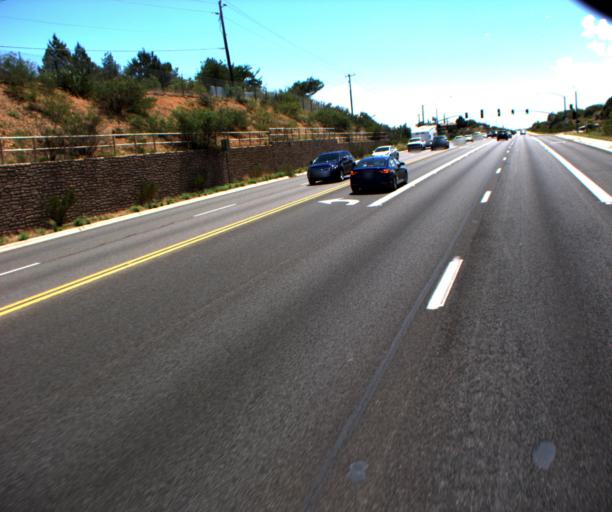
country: US
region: Arizona
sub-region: Yavapai County
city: Verde Village
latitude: 34.7004
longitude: -111.9881
